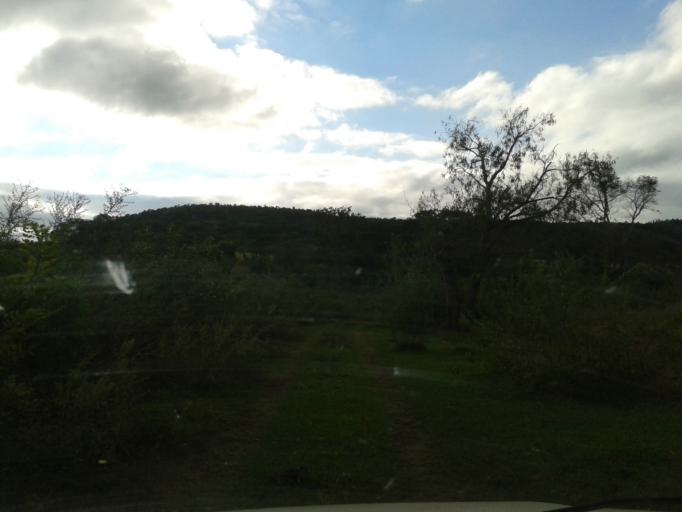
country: BR
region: Minas Gerais
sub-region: Campina Verde
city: Campina Verde
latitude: -19.4639
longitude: -49.6327
